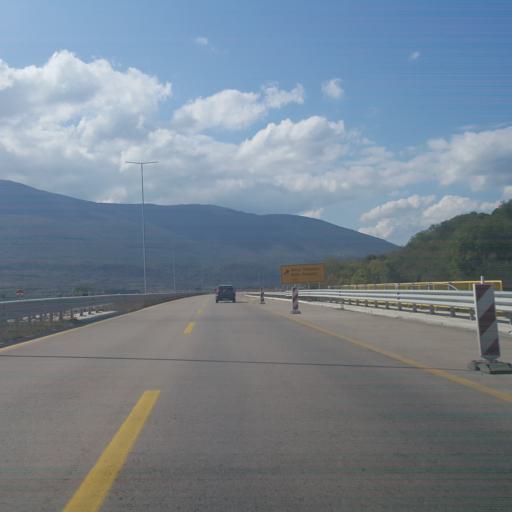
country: RS
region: Central Serbia
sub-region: Pirotski Okrug
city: Bela Palanka
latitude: 43.2356
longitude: 22.3193
